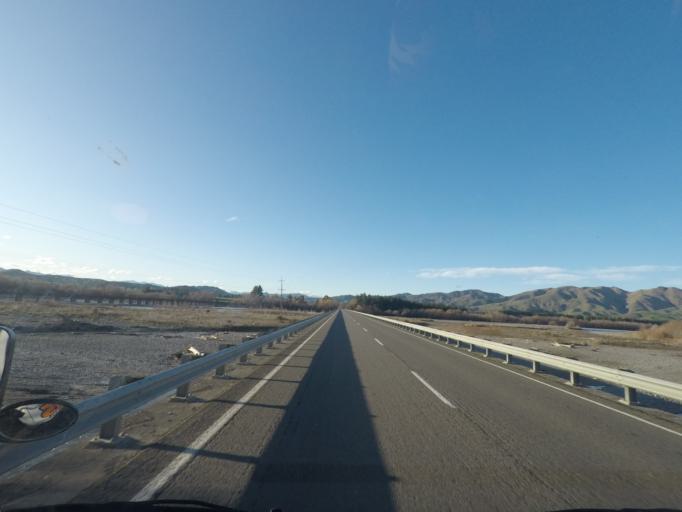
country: NZ
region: Canterbury
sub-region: Kaikoura District
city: Kaikoura
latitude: -42.7239
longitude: 173.2821
